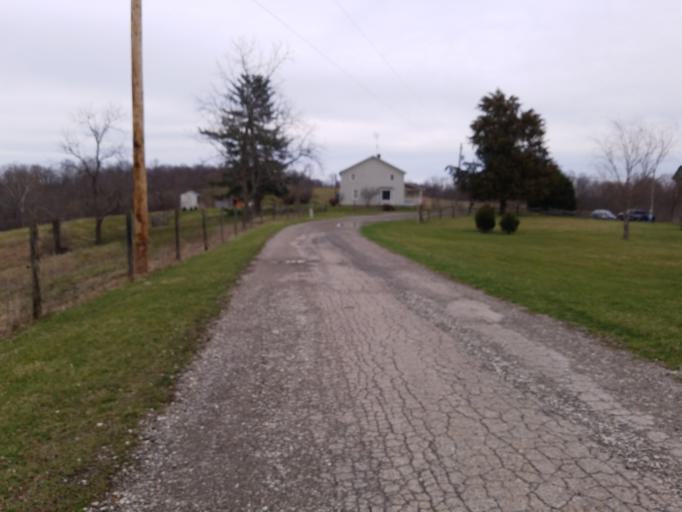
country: US
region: Ohio
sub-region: Morgan County
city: McConnelsville
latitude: 39.5060
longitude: -81.8758
